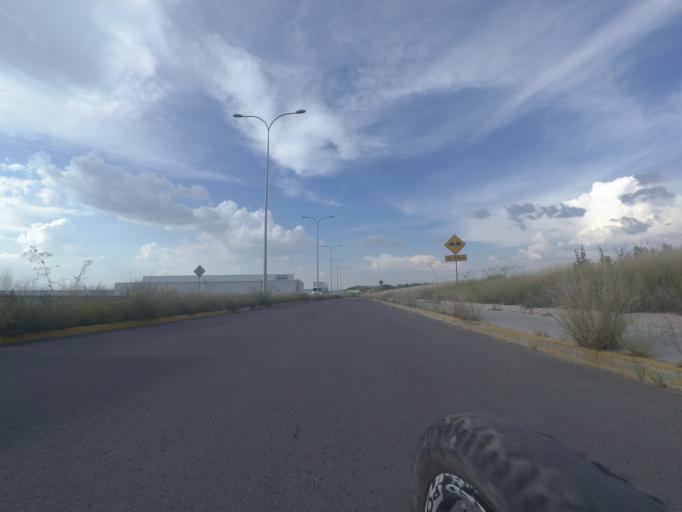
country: MX
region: Aguascalientes
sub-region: Aguascalientes
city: Penuelas (El Cienegal)
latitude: 21.7255
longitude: -102.2882
